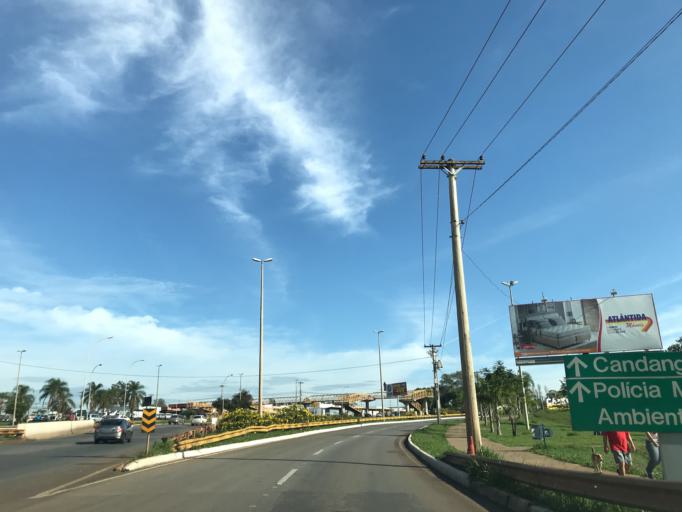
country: BR
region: Federal District
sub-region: Brasilia
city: Brasilia
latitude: -15.8600
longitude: -47.9555
